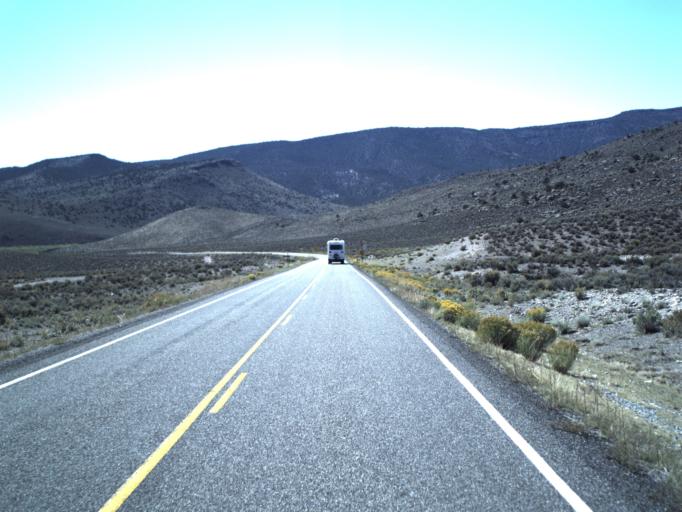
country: US
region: Utah
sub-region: Piute County
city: Junction
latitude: 38.1763
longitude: -112.0236
